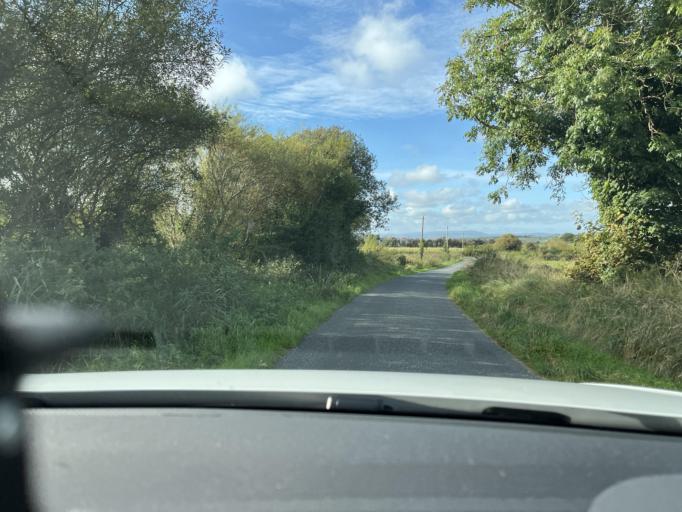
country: IE
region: Connaught
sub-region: Sligo
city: Ballymote
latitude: 54.0774
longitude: -8.4490
